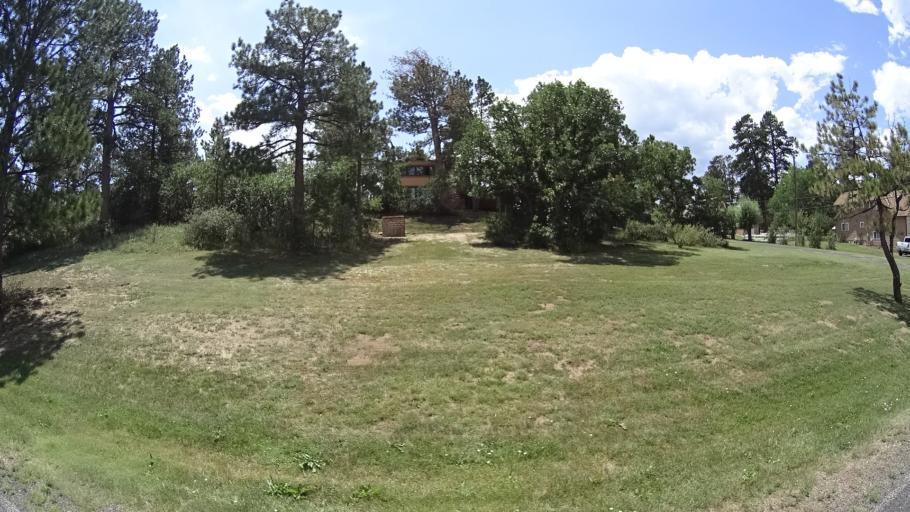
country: US
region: Colorado
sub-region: El Paso County
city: Air Force Academy
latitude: 38.9346
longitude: -104.8047
